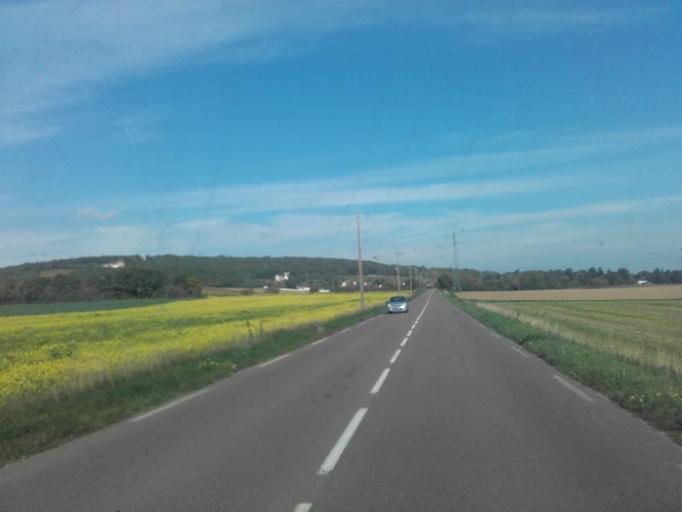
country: FR
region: Bourgogne
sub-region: Departement de Saone-et-Loire
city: Fontaines
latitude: 46.8382
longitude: 4.7523
